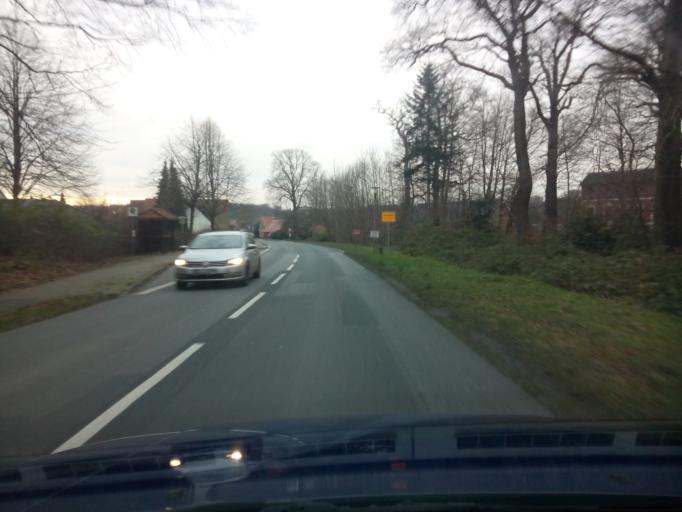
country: DE
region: Lower Saxony
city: Drangstedt
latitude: 53.6162
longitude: 8.7582
